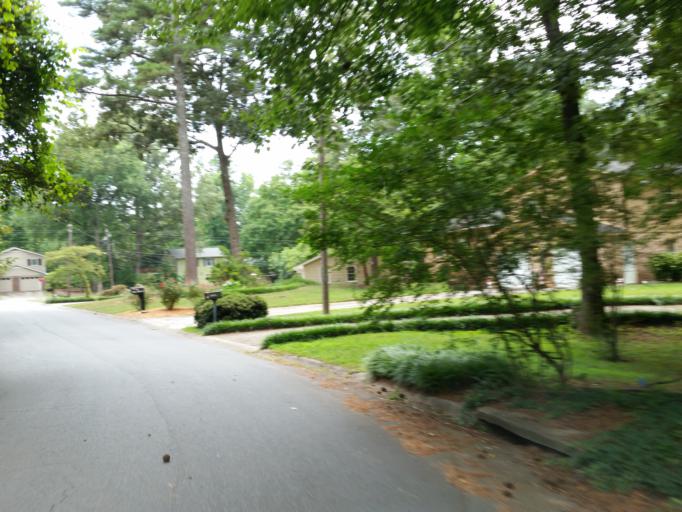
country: US
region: Georgia
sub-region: Cherokee County
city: Woodstock
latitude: 34.0209
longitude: -84.4769
